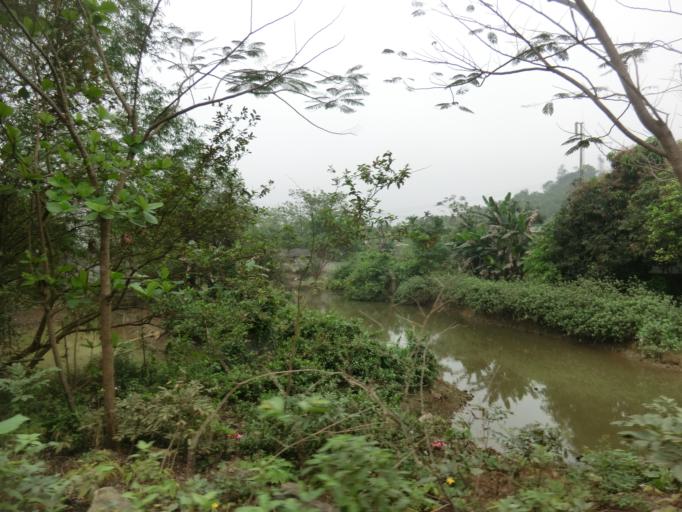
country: VN
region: Ninh Binh
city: Thi Tran Nho Quan
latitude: 20.2745
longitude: 105.7398
